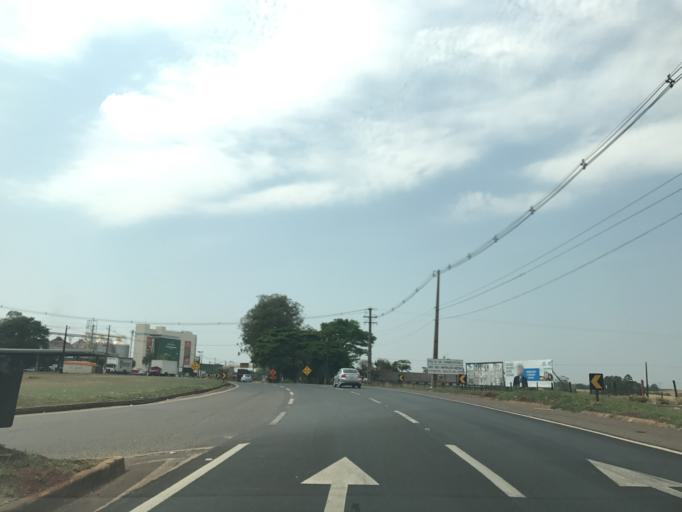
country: BR
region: Parana
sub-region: Rolandia
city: Rolandia
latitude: -23.3582
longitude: -51.3961
